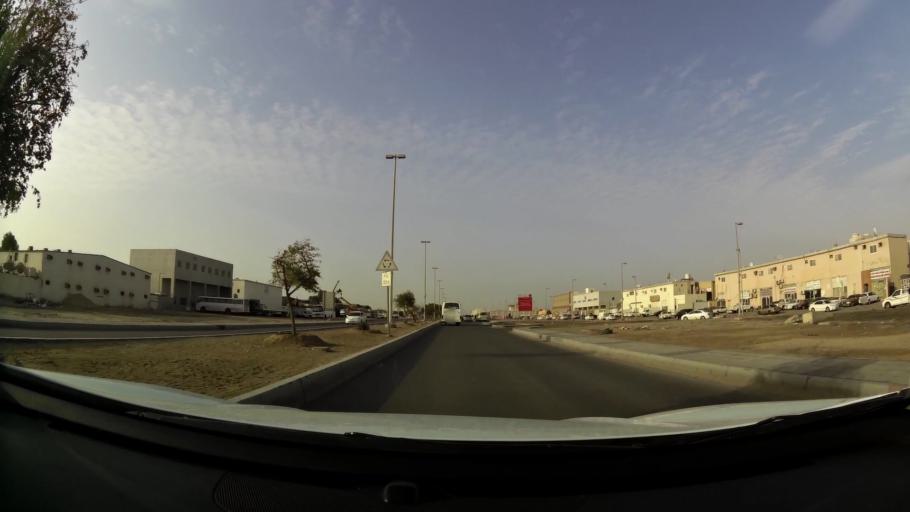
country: AE
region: Abu Dhabi
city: Abu Dhabi
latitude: 24.3523
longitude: 54.5170
